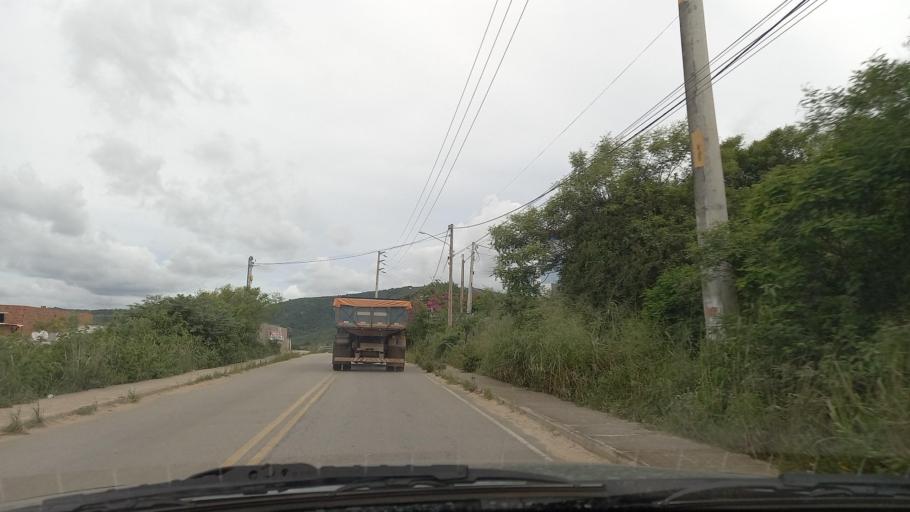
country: BR
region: Pernambuco
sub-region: Gravata
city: Gravata
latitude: -8.2194
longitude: -35.5763
